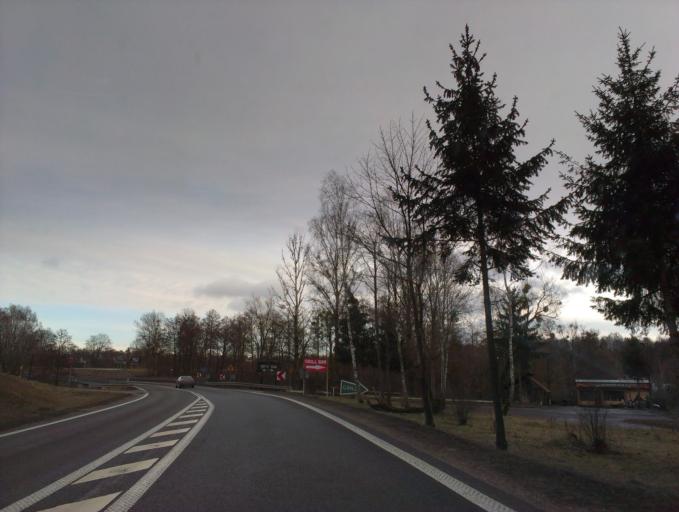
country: PL
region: Masovian Voivodeship
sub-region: Powiat sierpecki
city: Sierpc
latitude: 52.8685
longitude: 19.6302
